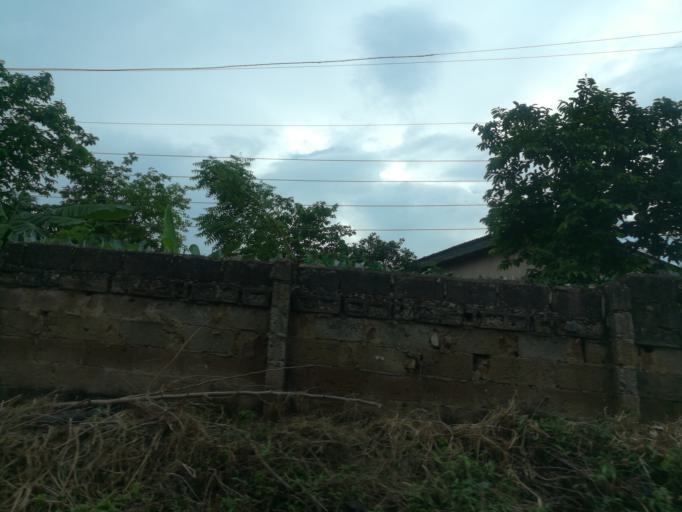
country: NG
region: Oyo
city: Ibadan
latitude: 7.4155
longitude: 3.9069
